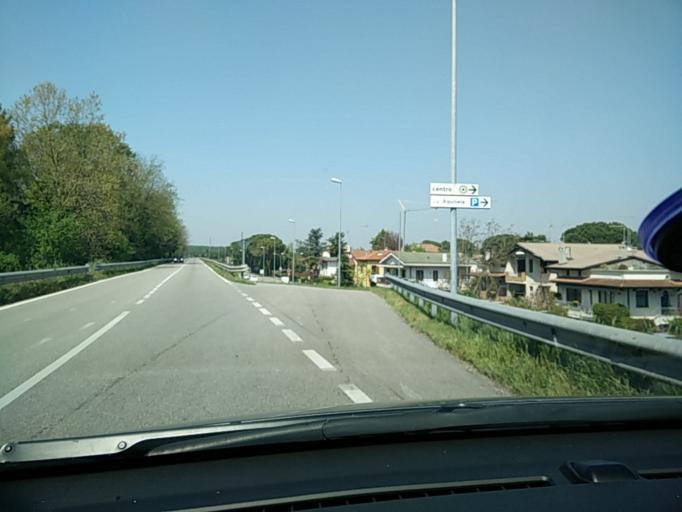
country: IT
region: Veneto
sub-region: Provincia di Venezia
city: San Dona di Piave
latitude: 45.6298
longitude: 12.5593
